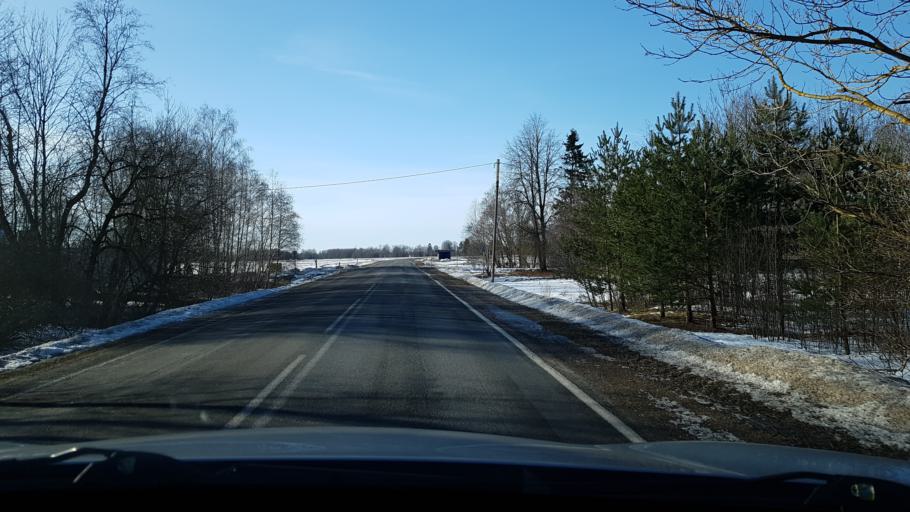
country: EE
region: Viljandimaa
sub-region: Vohma linn
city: Vohma
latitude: 58.6340
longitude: 25.6475
